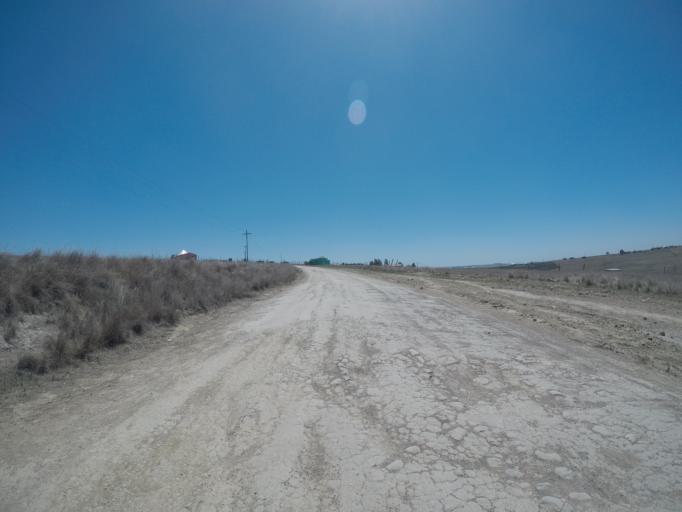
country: ZA
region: Eastern Cape
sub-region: OR Tambo District Municipality
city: Mthatha
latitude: -31.8979
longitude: 28.8966
